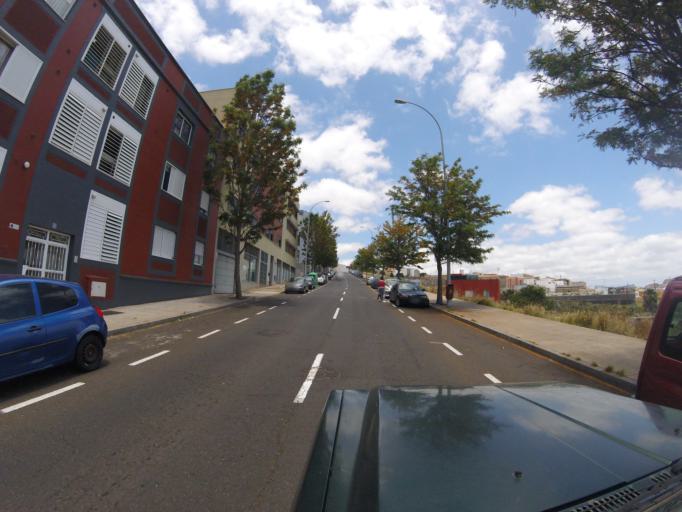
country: ES
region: Canary Islands
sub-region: Provincia de Santa Cruz de Tenerife
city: La Laguna
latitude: 28.4321
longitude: -16.3101
